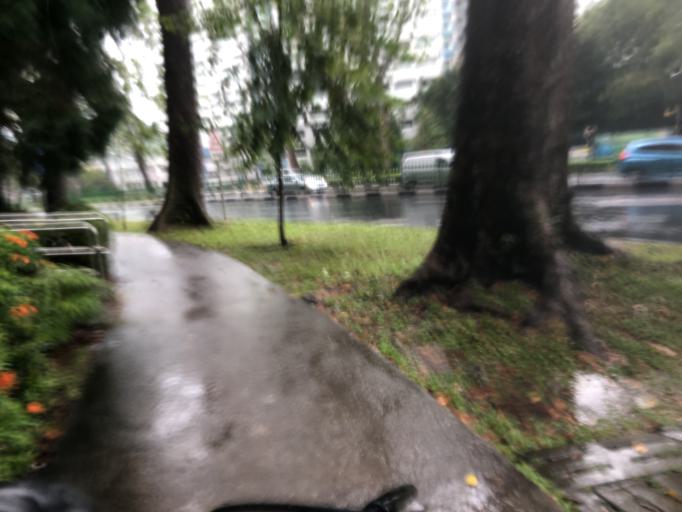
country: SG
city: Singapore
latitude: 1.3455
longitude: 103.7579
